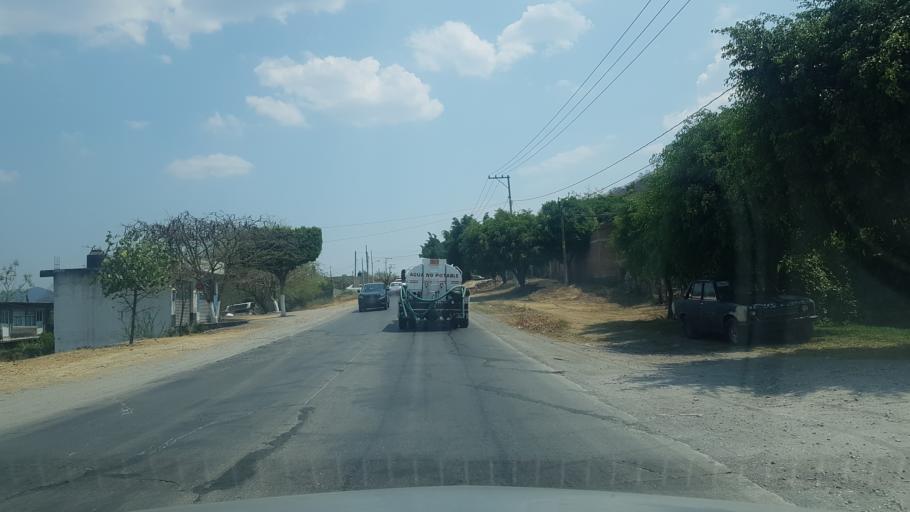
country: MX
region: Morelos
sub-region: Tlaltizapan de Zapata
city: Colonia Palo Prieto (Chipitongo)
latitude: 18.7123
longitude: -99.1178
